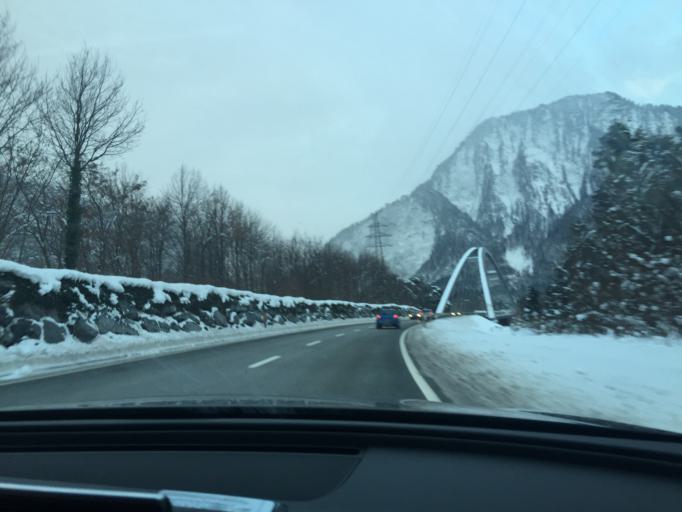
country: CH
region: Grisons
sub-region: Landquart District
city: Malans
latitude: 46.9701
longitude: 9.5726
